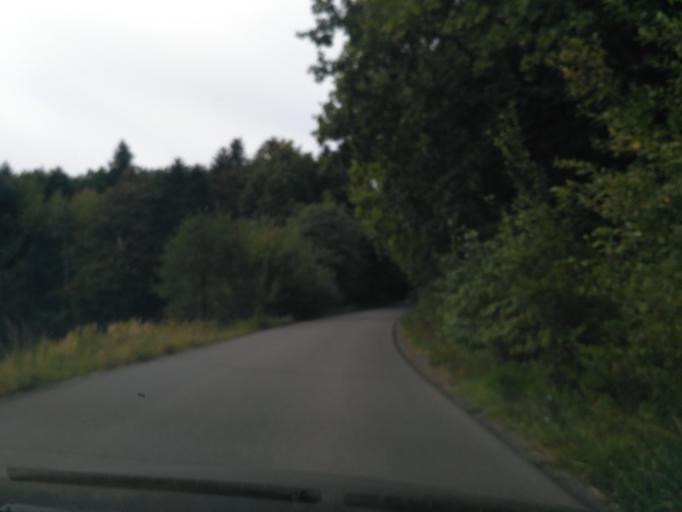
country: PL
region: Subcarpathian Voivodeship
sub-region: Powiat strzyzowski
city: Czudec
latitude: 49.9644
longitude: 21.8419
